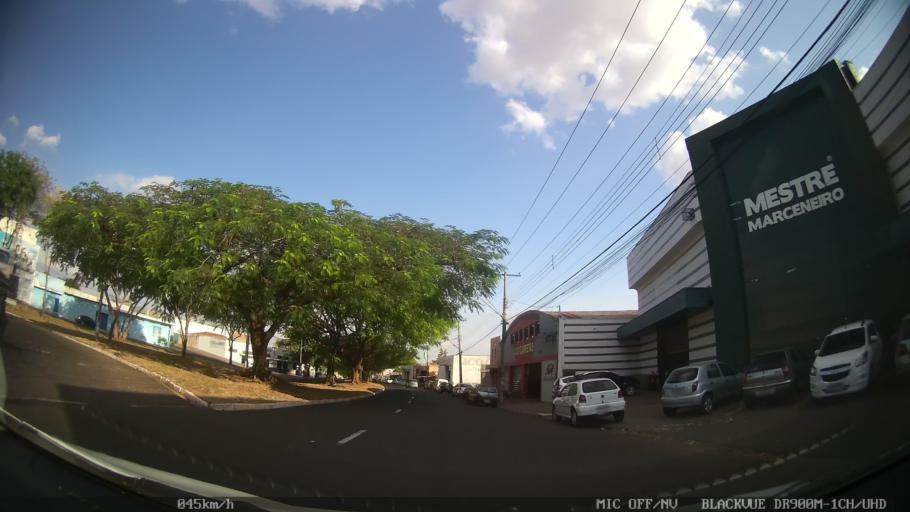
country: BR
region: Sao Paulo
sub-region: Ribeirao Preto
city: Ribeirao Preto
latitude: -21.1426
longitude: -47.7996
